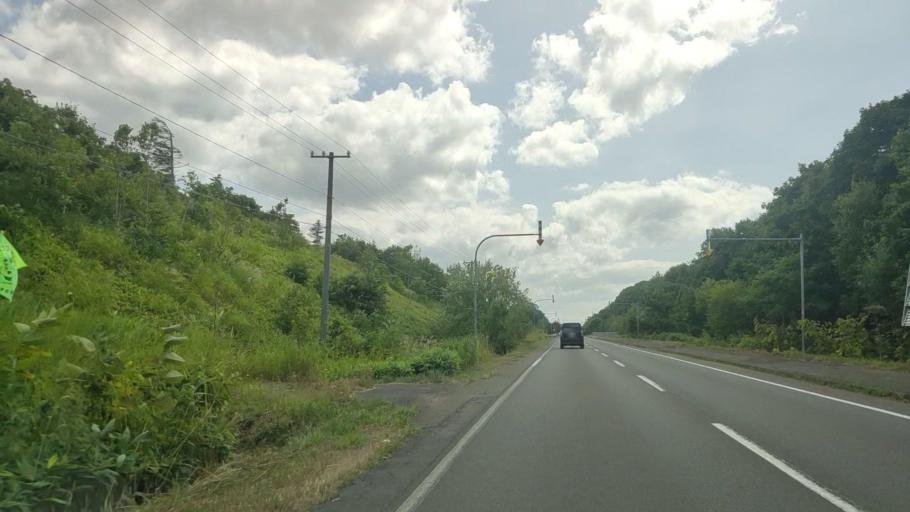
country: JP
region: Hokkaido
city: Makubetsu
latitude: 44.7672
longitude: 141.7931
